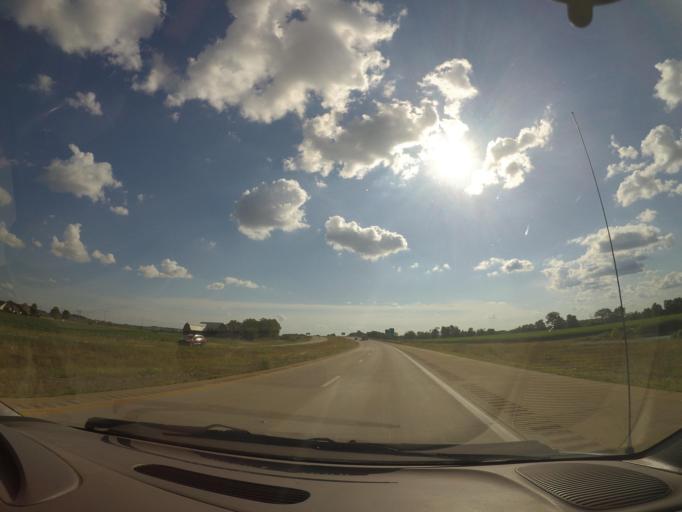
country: US
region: Ohio
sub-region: Lucas County
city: Waterville
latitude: 41.5240
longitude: -83.7365
